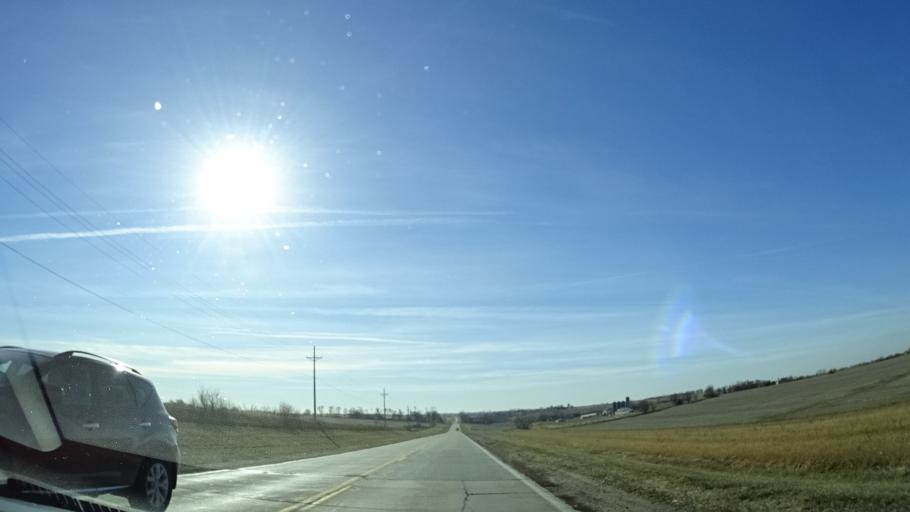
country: US
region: Nebraska
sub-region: Sarpy County
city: Papillion
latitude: 41.1143
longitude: -96.0429
